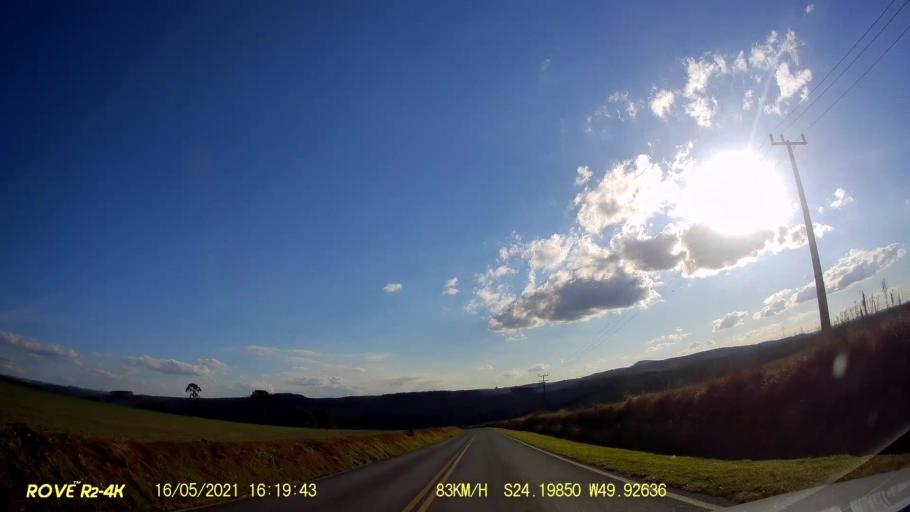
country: BR
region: Parana
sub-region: Jaguariaiva
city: Jaguariaiva
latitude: -24.1991
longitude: -49.9262
